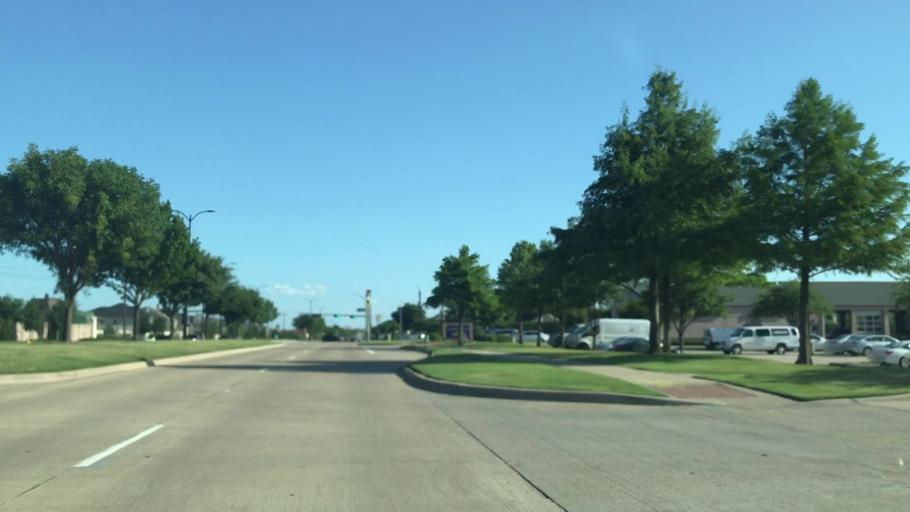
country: US
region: Texas
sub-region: Collin County
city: Frisco
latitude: 33.1320
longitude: -96.7681
